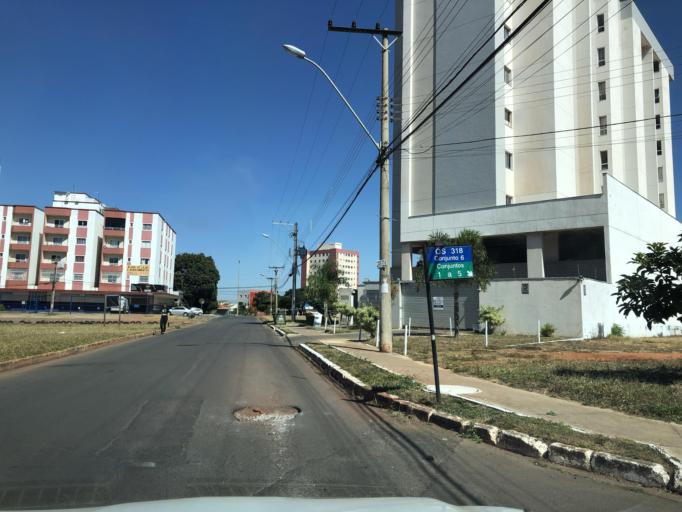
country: BR
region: Federal District
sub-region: Brasilia
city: Brasilia
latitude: -15.8750
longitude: -48.0613
